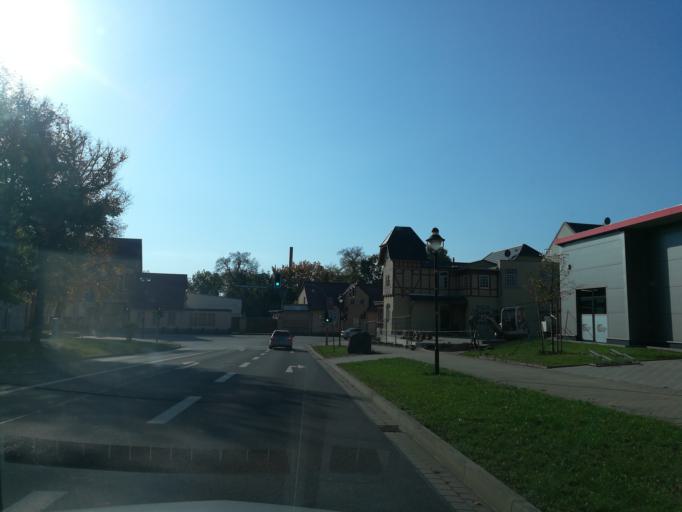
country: DE
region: Saxony-Anhalt
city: Gommern
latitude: 52.0738
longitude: 11.8252
